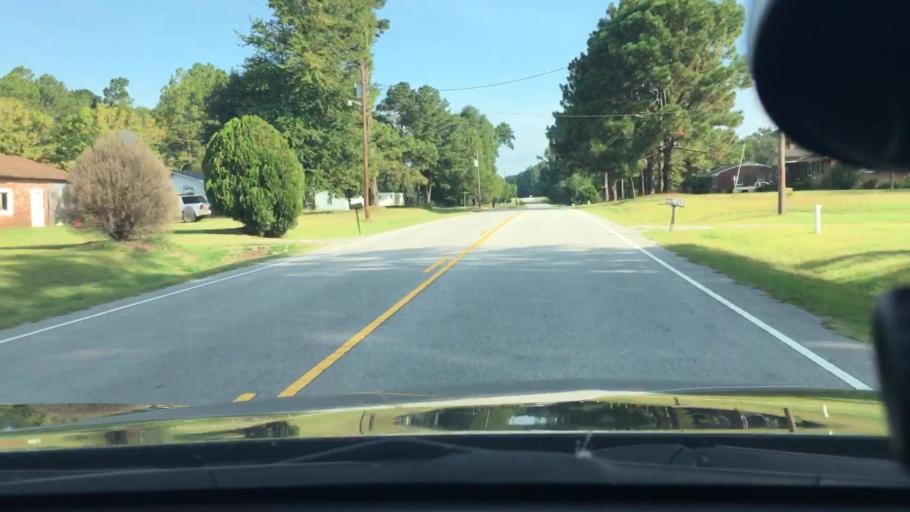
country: US
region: North Carolina
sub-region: Edgecombe County
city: Pinetops
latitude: 35.7271
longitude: -77.5314
